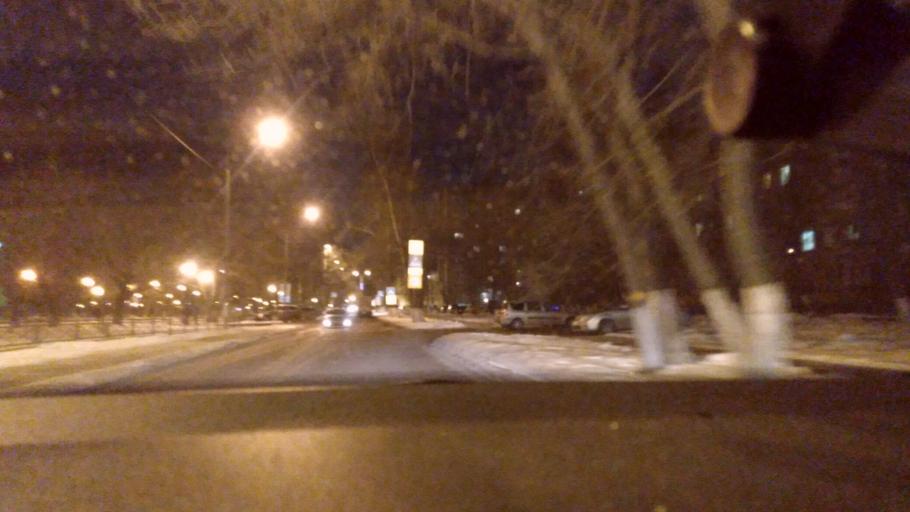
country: RU
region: Moskovskaya
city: Zheleznodorozhnyy
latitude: 55.7500
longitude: 38.0169
